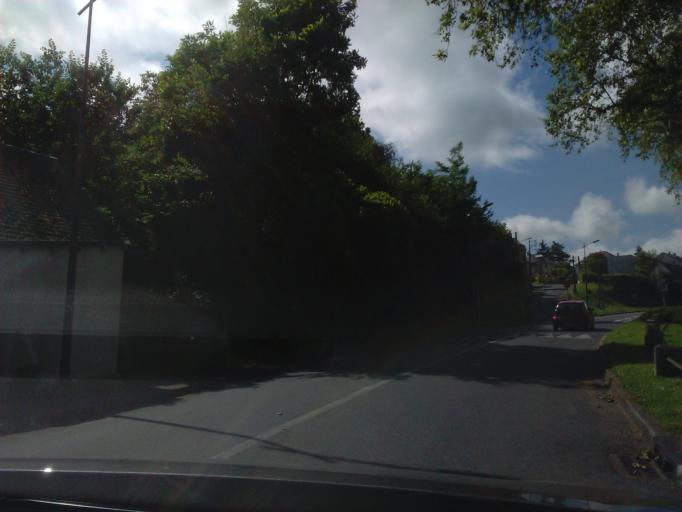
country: FR
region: Centre
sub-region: Departement du Loir-et-Cher
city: Vendome
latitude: 47.7866
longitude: 1.0639
